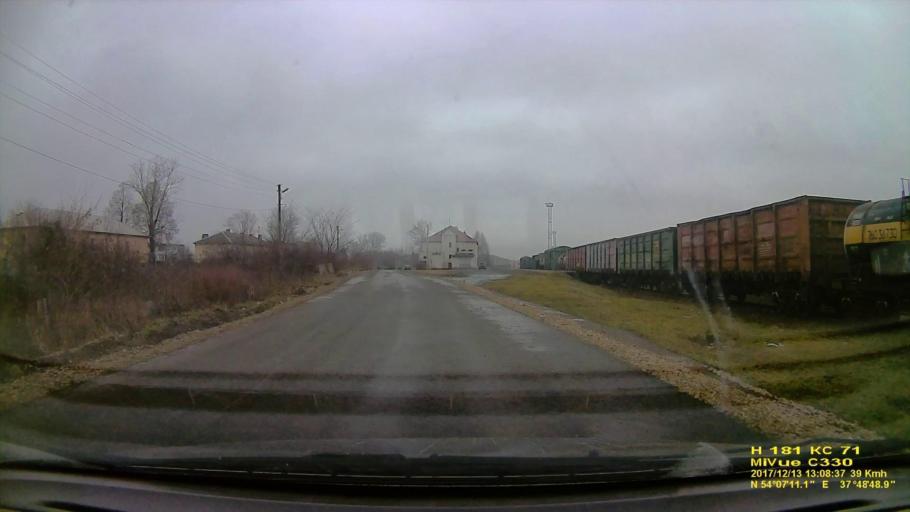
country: RU
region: Tula
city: Bolokhovo
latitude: 54.1197
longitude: 37.8139
